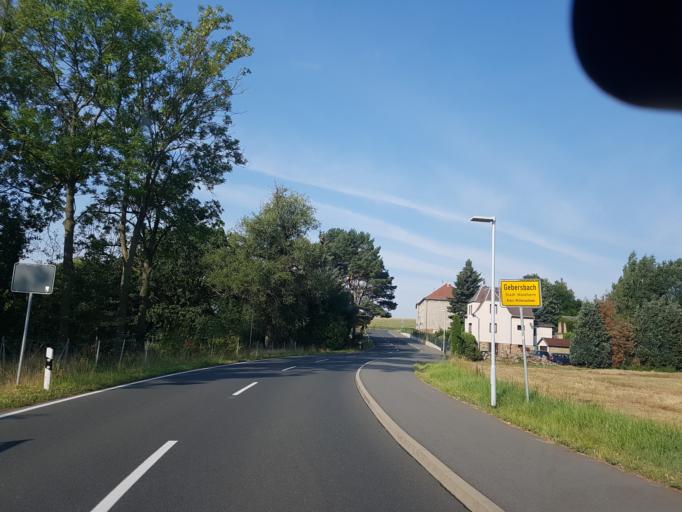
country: DE
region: Saxony
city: Ebersbach
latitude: 51.0879
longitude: 13.0724
